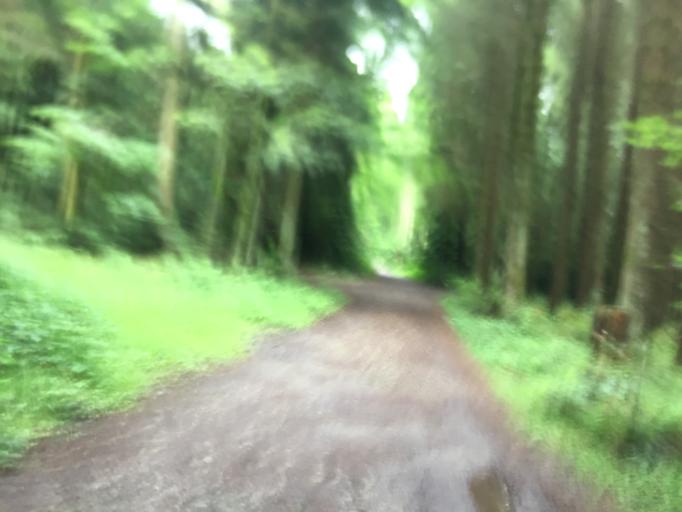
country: CH
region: Bern
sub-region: Bern-Mittelland District
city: Stettlen
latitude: 46.9264
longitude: 7.5212
